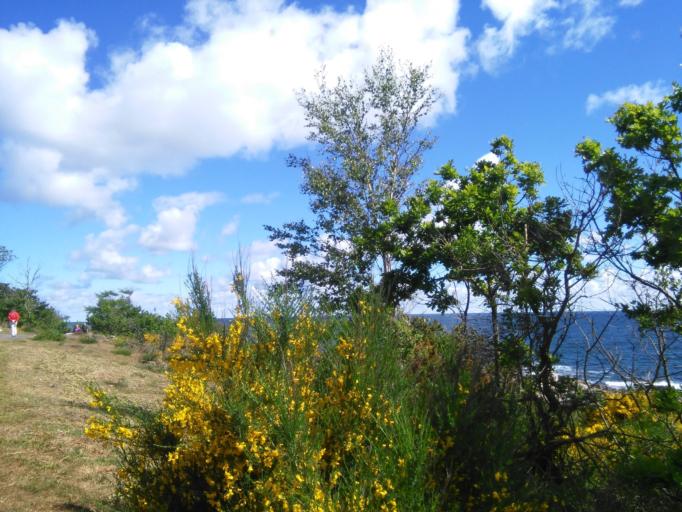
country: DK
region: Capital Region
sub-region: Bornholm Kommune
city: Ronne
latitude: 55.2942
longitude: 14.7776
